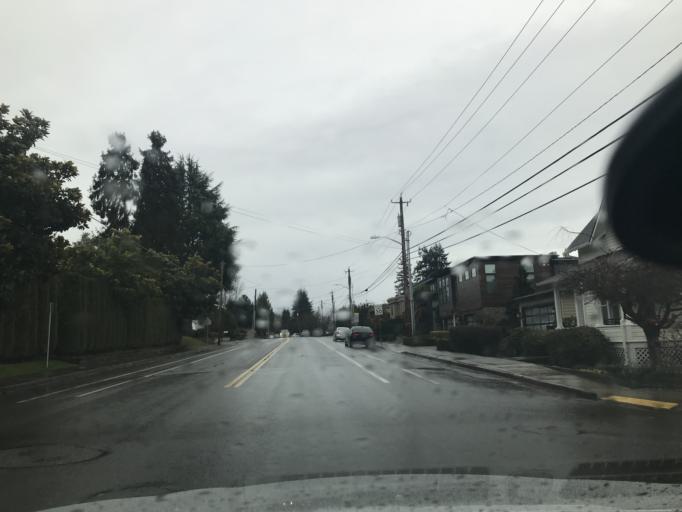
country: US
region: Washington
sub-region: King County
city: Kirkland
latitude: 47.6705
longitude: -122.2023
